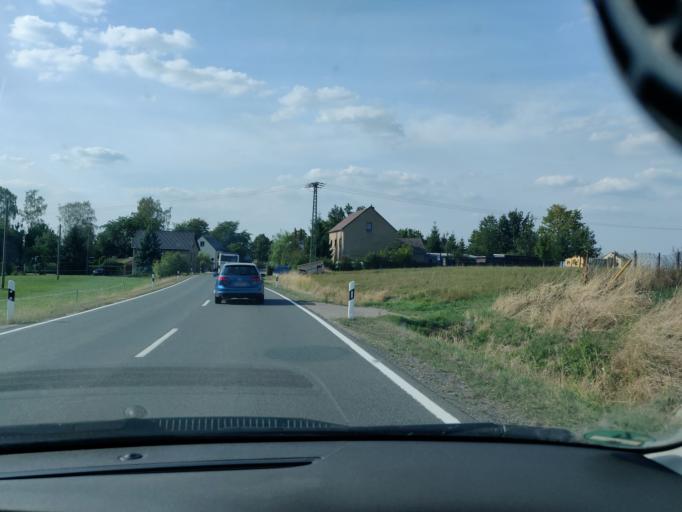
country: DE
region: Saxony
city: Seelitz
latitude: 51.0345
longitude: 12.8280
